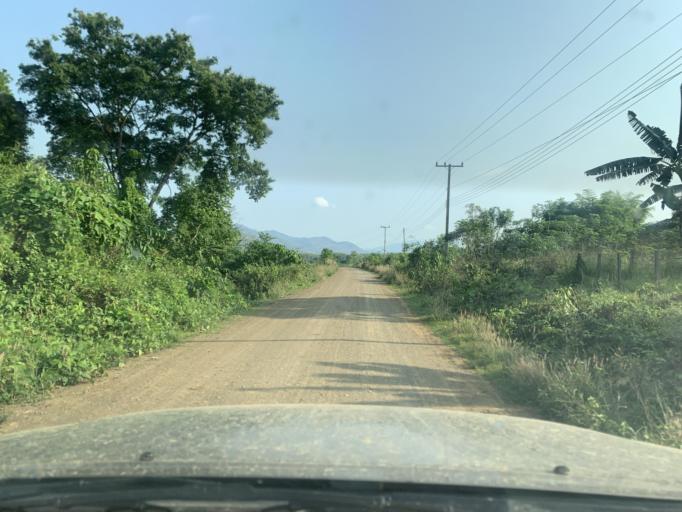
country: TH
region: Uttaradit
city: Ban Khok
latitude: 18.2751
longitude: 101.3061
